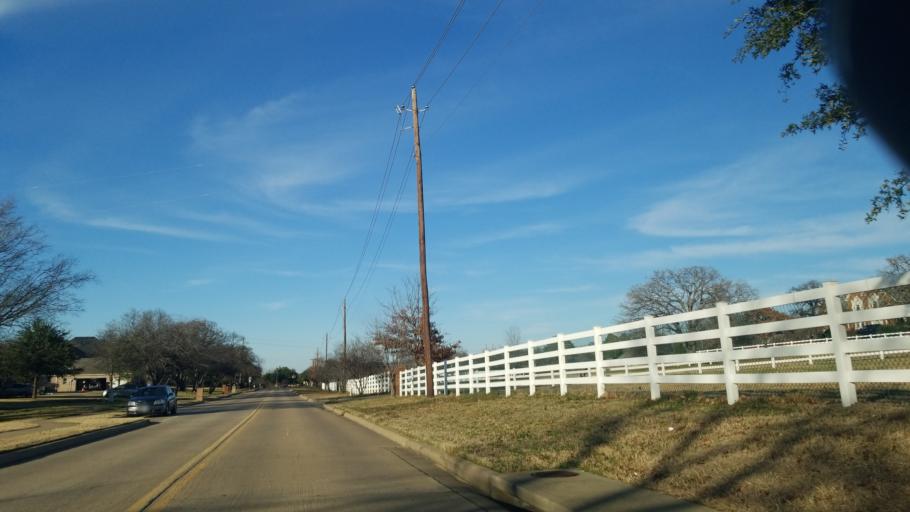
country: US
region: Texas
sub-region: Denton County
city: Corinth
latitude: 33.1521
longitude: -97.0788
